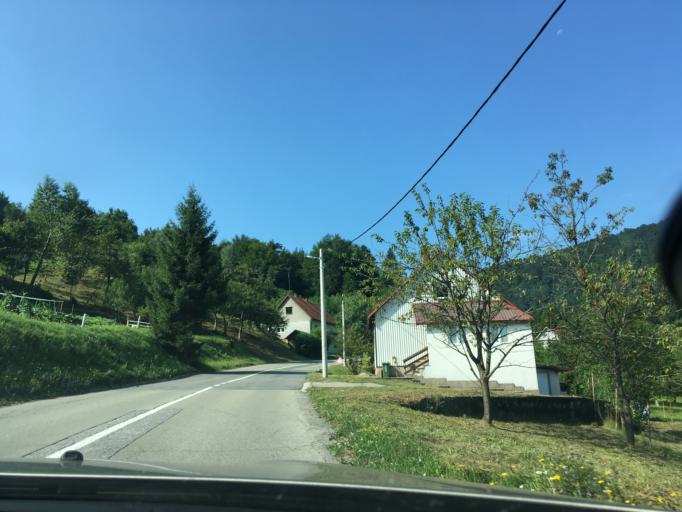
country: HR
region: Primorsko-Goranska
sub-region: Grad Delnice
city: Delnice
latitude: 45.4189
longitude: 14.8241
